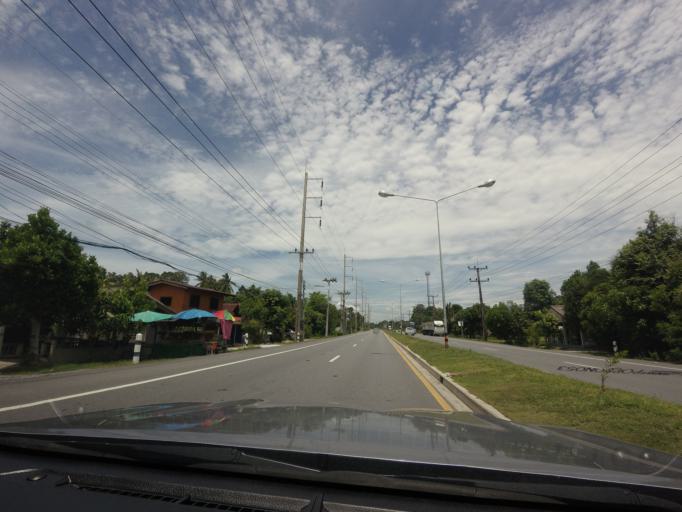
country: TH
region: Songkhla
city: Krasae Sin
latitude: 7.5742
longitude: 100.4094
